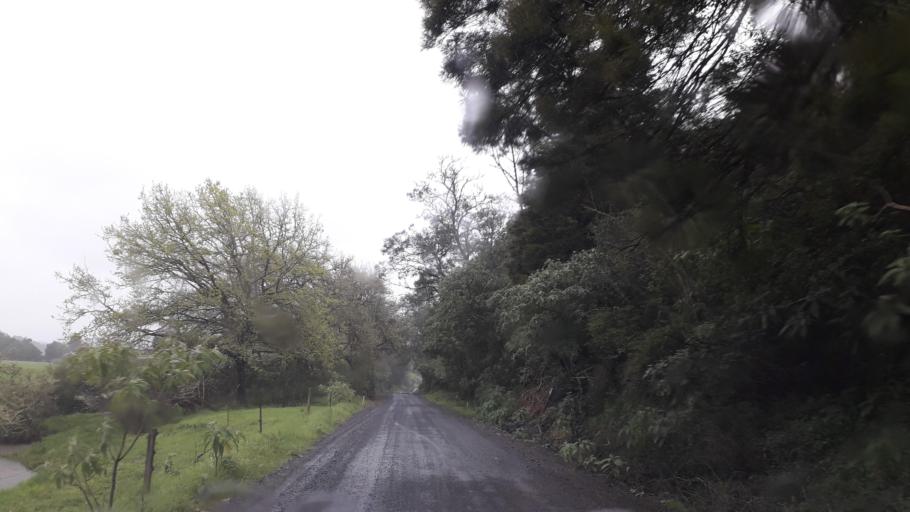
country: NZ
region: Northland
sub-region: Far North District
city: Waimate North
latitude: -35.4796
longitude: 173.6973
